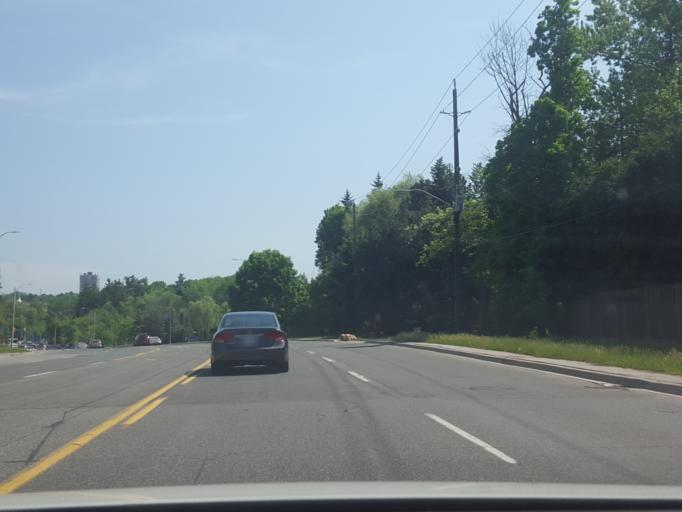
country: CA
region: Ontario
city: Willowdale
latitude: 43.8058
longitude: -79.3981
